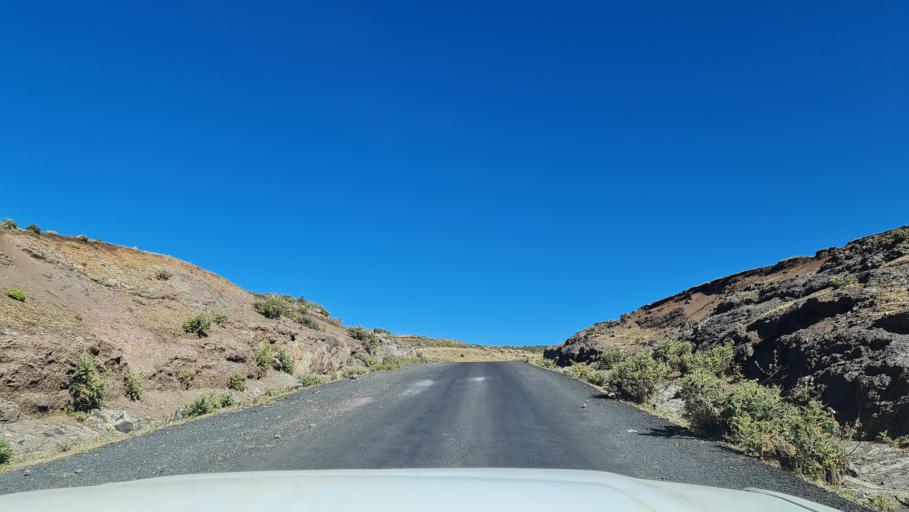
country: ET
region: Amhara
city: Debark'
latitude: 13.1371
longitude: 38.1781
